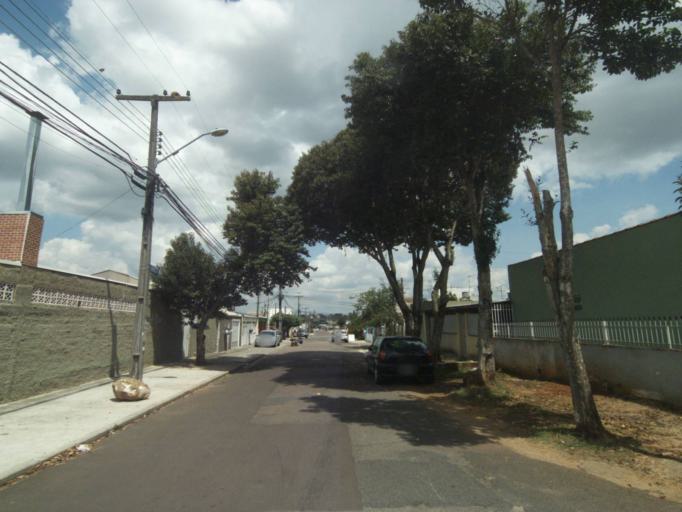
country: BR
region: Parana
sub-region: Sao Jose Dos Pinhais
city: Sao Jose dos Pinhais
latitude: -25.5389
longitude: -49.2726
